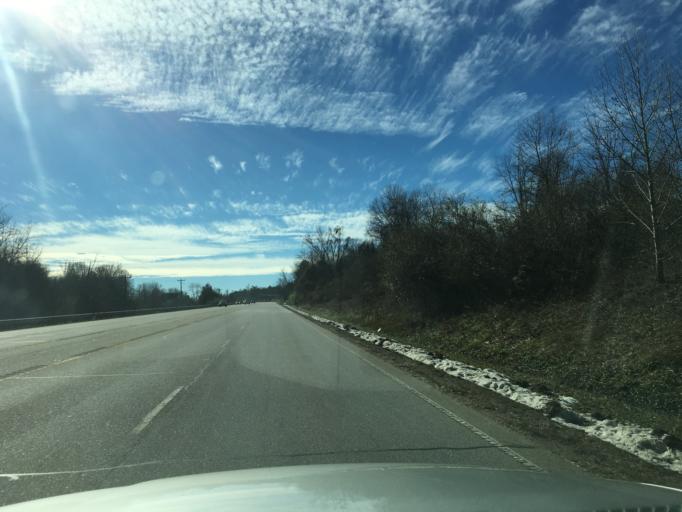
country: US
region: North Carolina
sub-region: Henderson County
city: Mills River
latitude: 35.3694
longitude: -82.5906
